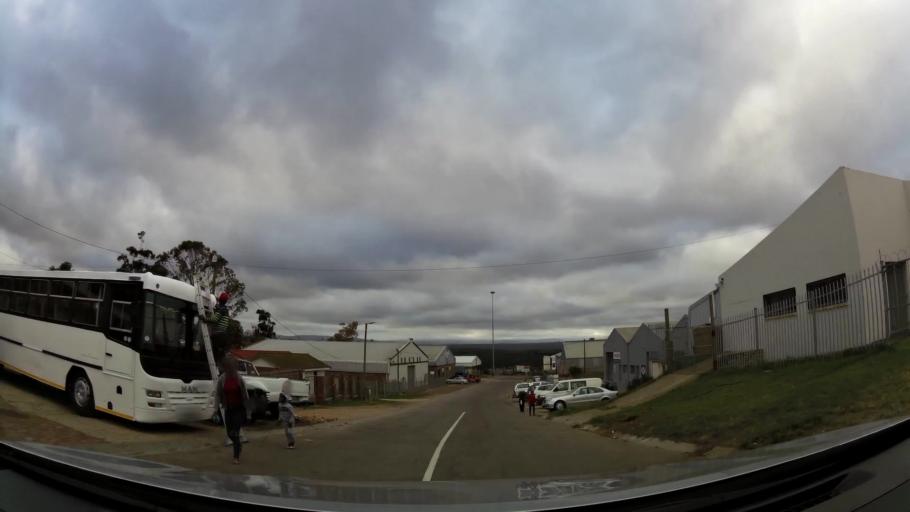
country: ZA
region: Western Cape
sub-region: Eden District Municipality
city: Plettenberg Bay
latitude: -34.0496
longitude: 23.3534
